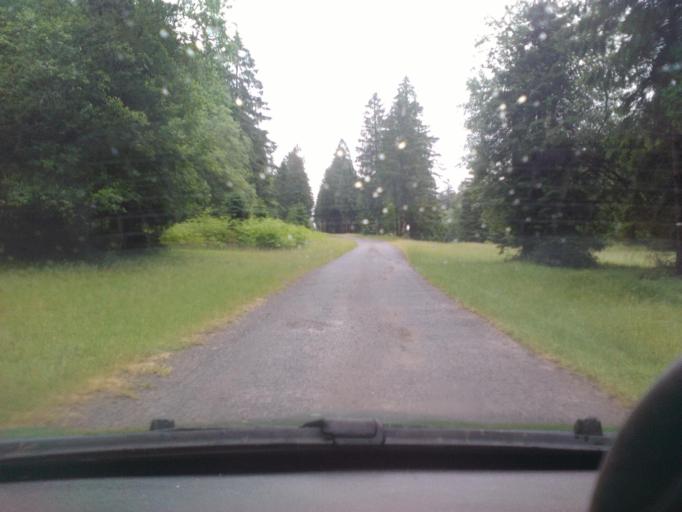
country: FR
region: Alsace
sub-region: Departement du Bas-Rhin
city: Rothau
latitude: 48.4786
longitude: 7.1031
